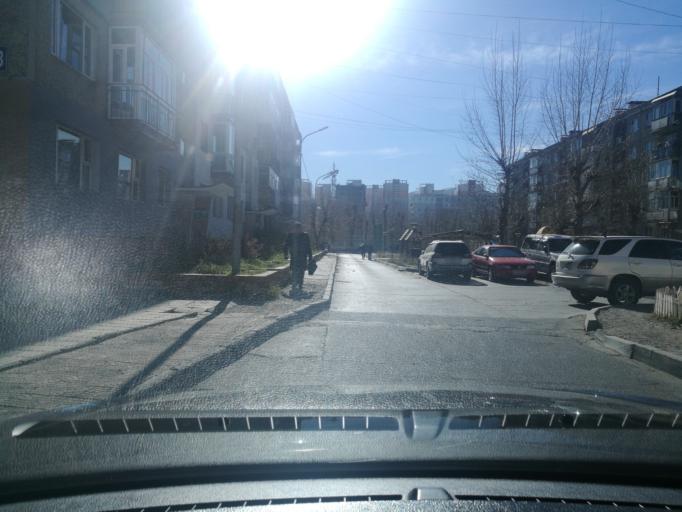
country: MN
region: Ulaanbaatar
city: Ulaanbaatar
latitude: 47.9123
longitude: 106.8978
